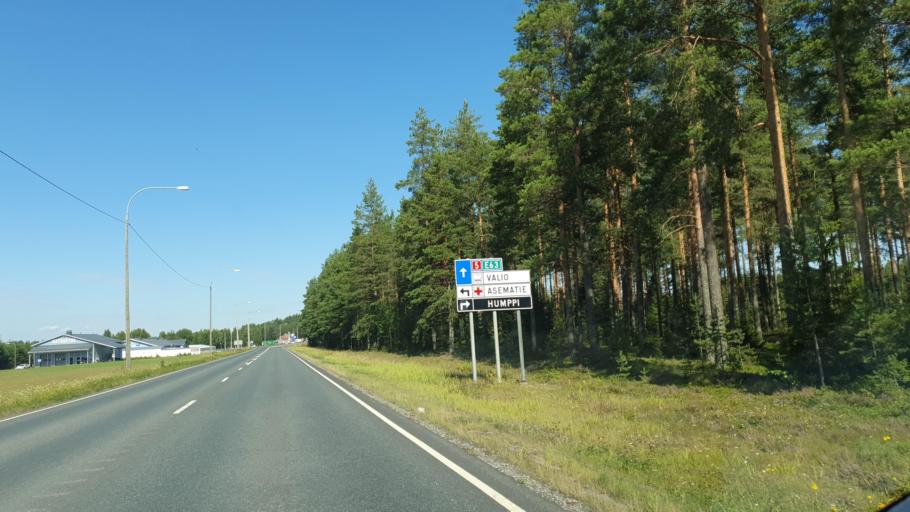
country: FI
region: Northern Savo
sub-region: Ylae-Savo
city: Lapinlahti
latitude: 63.3435
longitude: 27.4191
